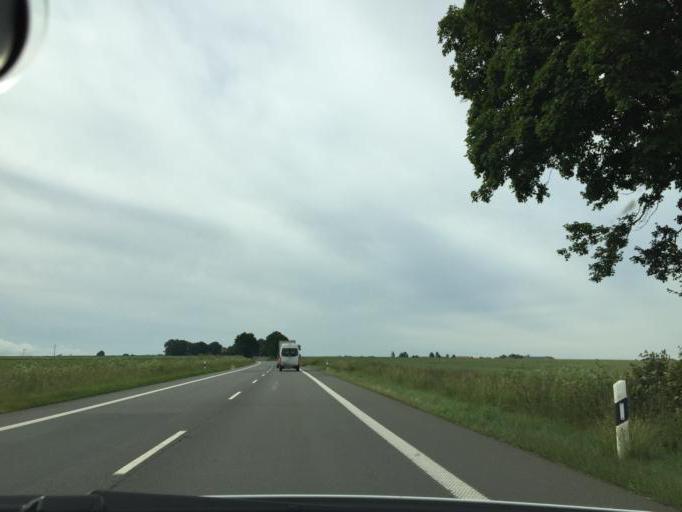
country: DE
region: North Rhine-Westphalia
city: Warburg
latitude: 51.5467
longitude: 9.1325
